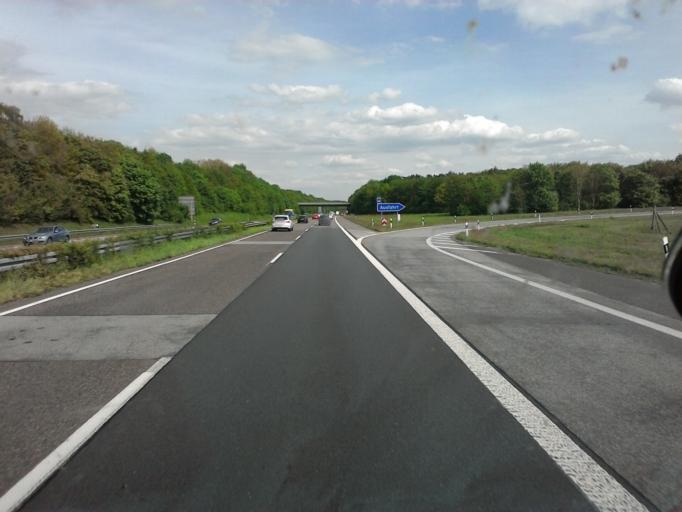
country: DE
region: North Rhine-Westphalia
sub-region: Regierungsbezirk Dusseldorf
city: Alpen
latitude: 51.5645
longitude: 6.4901
